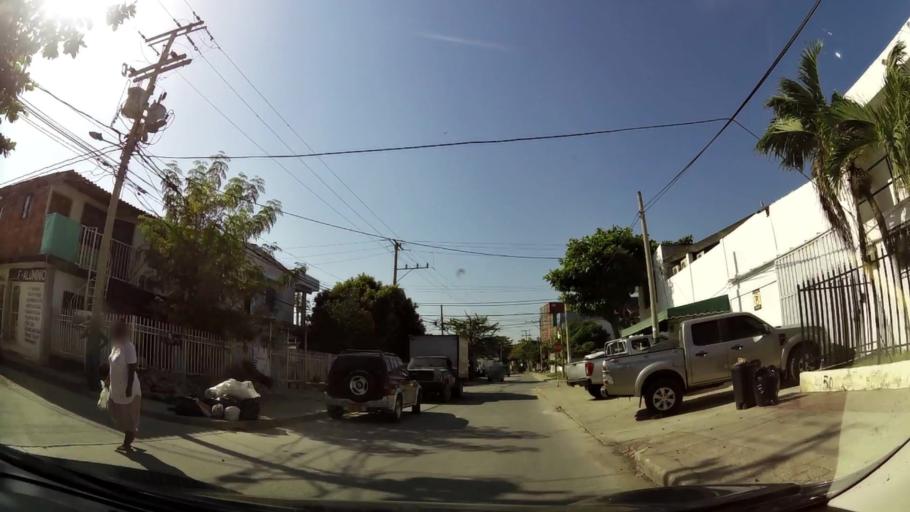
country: CO
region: Bolivar
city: Cartagena
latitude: 10.3720
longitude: -75.5034
